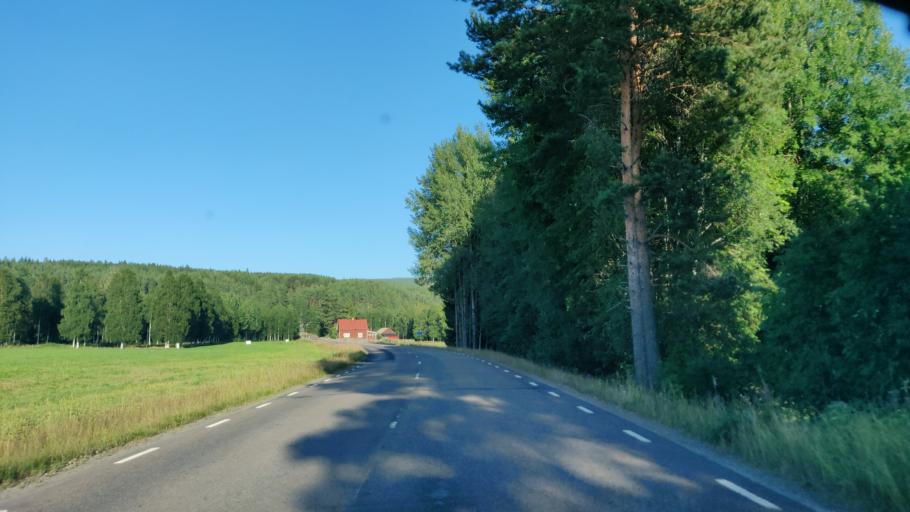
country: SE
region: Vaermland
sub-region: Hagfors Kommun
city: Ekshaerad
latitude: 60.1774
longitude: 13.5197
